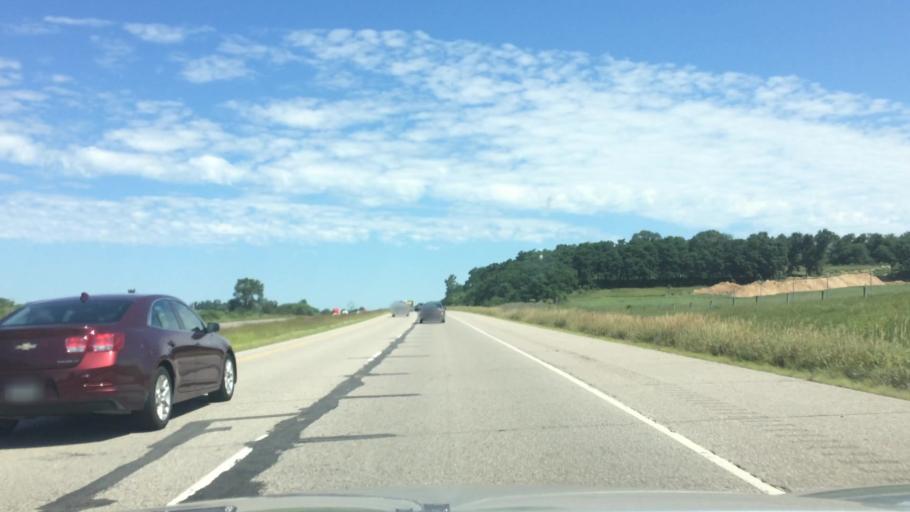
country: US
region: Wisconsin
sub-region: Columbia County
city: Portage
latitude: 43.6933
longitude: -89.4697
